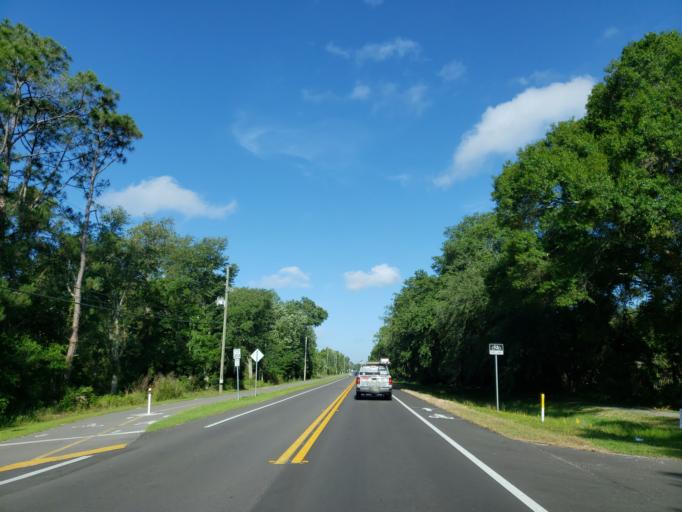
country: US
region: Florida
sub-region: Pasco County
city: Trinity
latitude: 28.1447
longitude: -82.6771
